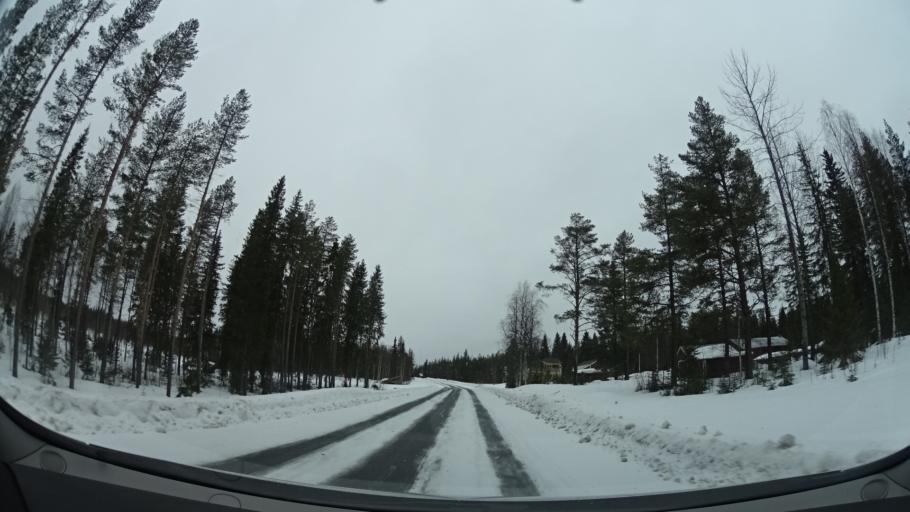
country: SE
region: Vaesterbotten
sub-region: Mala Kommun
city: Mala
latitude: 65.0823
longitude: 18.9959
